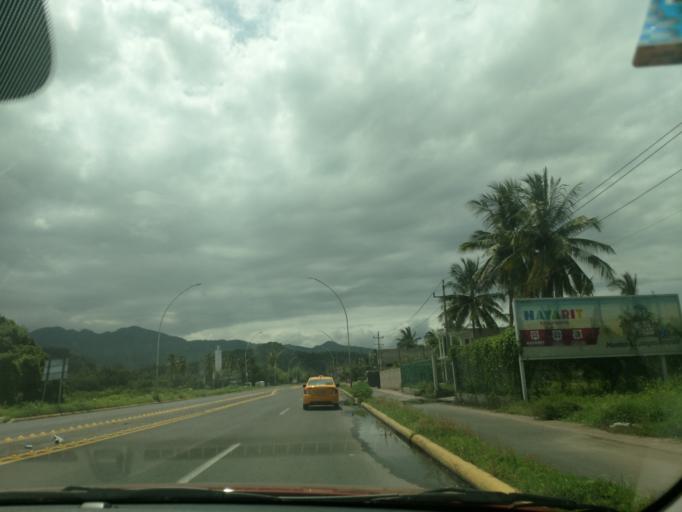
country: MX
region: Nayarit
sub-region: San Blas
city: Aticama
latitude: 21.5018
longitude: -105.2042
